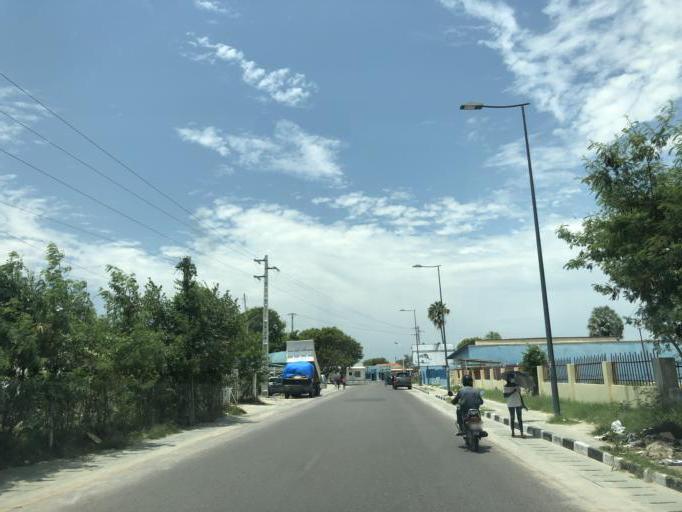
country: AO
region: Cunene
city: Ondjiva
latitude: -17.0683
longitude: 15.7294
